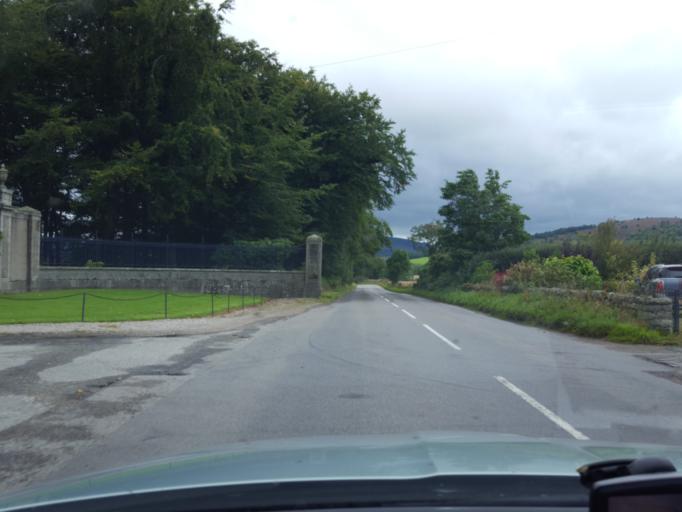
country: GB
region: Scotland
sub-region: Aberdeenshire
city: Kemnay
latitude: 57.1628
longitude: -2.4284
